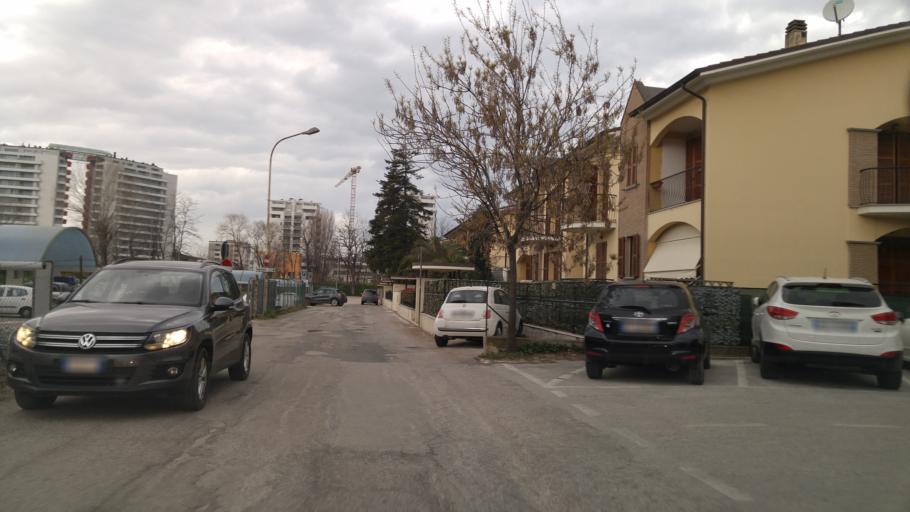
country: IT
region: The Marches
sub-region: Provincia di Pesaro e Urbino
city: Pesaro
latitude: 43.9029
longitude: 12.8940
